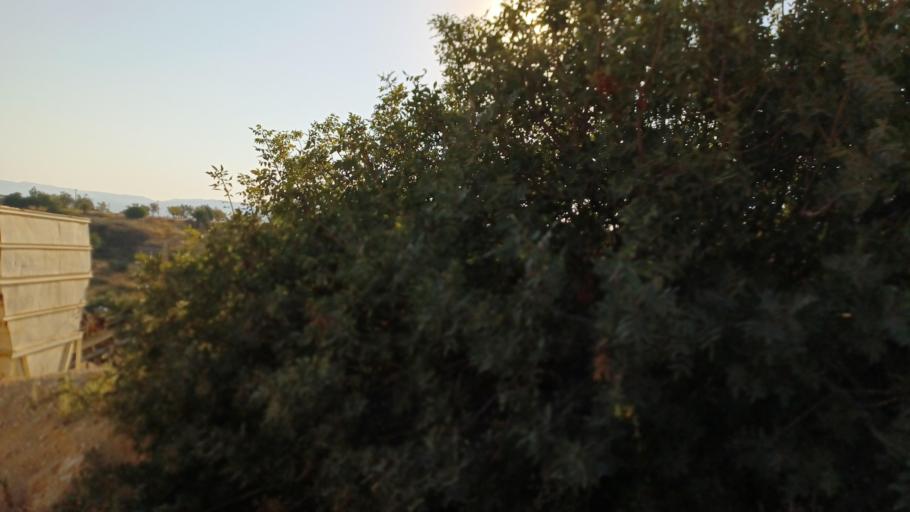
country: CY
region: Pafos
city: Polis
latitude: 35.0212
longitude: 32.3983
